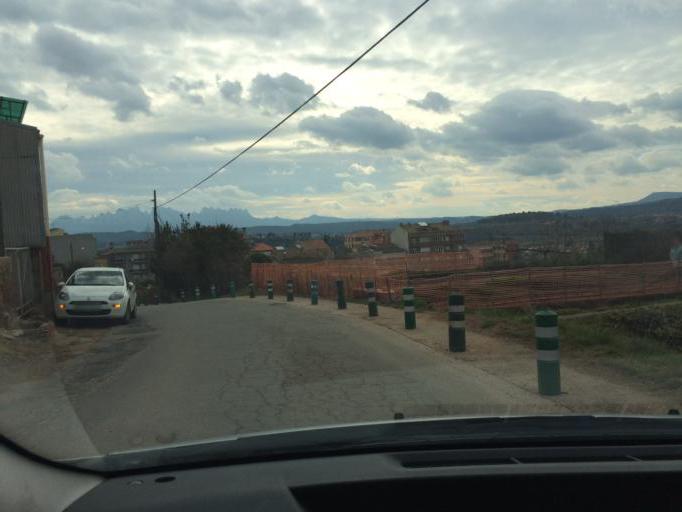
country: ES
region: Catalonia
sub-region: Provincia de Barcelona
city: Manresa
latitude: 41.7333
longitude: 1.8165
